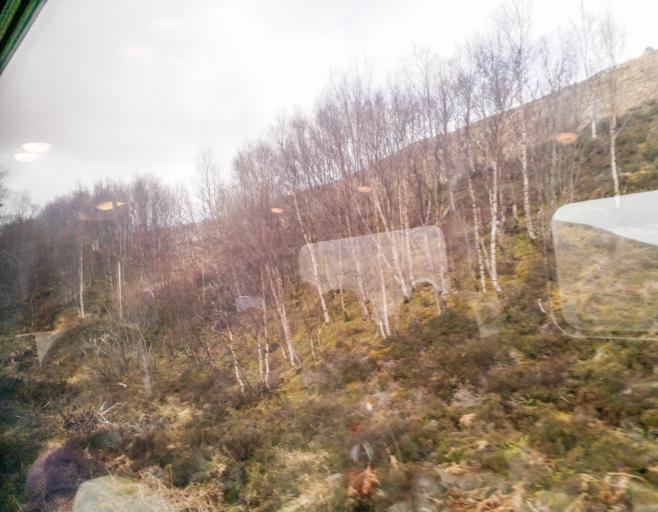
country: GB
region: Scotland
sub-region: Highland
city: Spean Bridge
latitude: 56.7816
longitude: -4.7330
